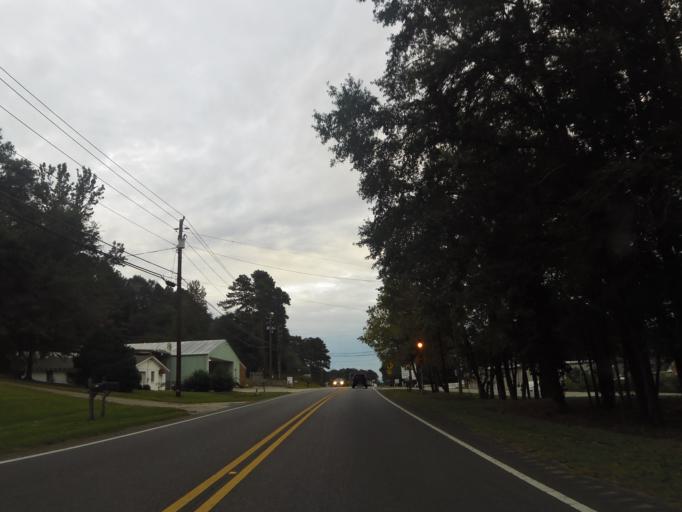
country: US
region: Alabama
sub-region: Jefferson County
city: Trussville
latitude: 33.6367
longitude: -86.5839
